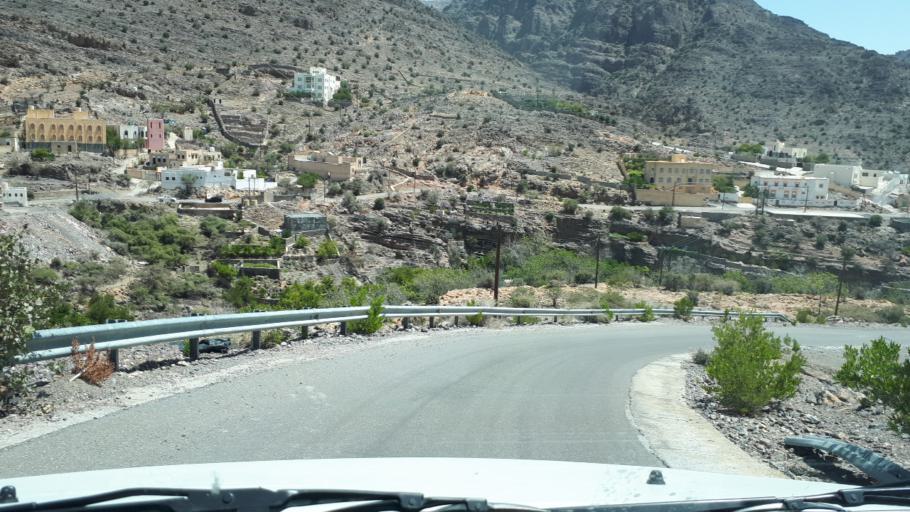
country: OM
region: Muhafazat ad Dakhiliyah
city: Izki
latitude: 23.0906
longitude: 57.7306
